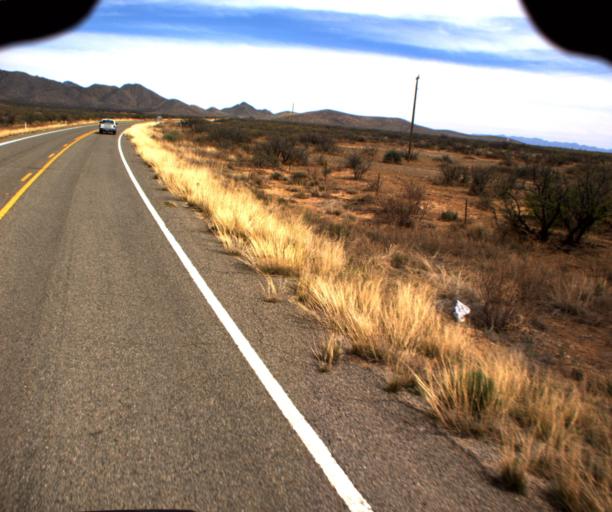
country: US
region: Arizona
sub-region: Cochise County
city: Willcox
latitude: 32.1952
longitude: -109.7108
